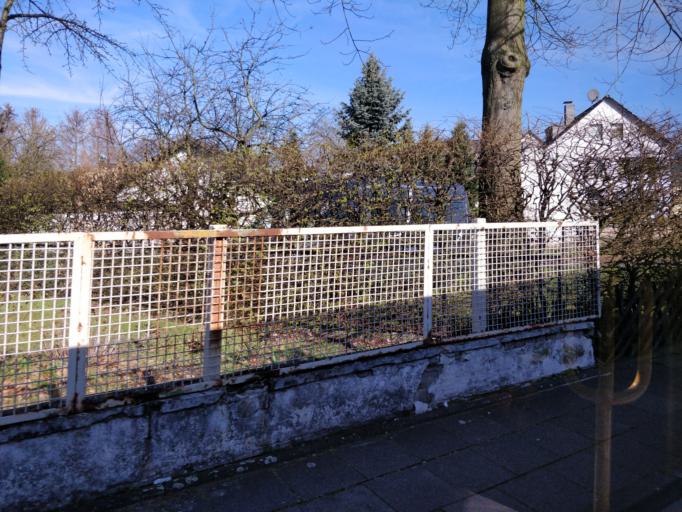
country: DE
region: North Rhine-Westphalia
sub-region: Regierungsbezirk Koln
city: Wahn-Heide
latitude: 50.8503
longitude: 7.1055
